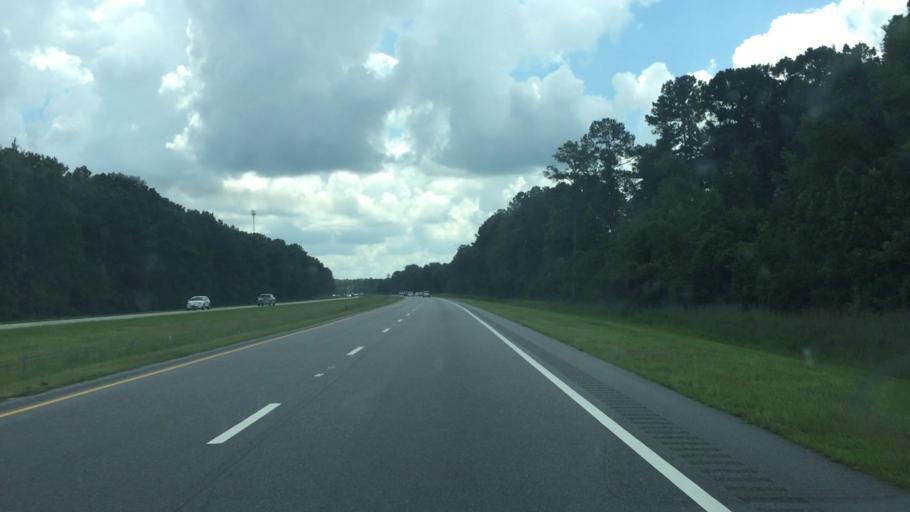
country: US
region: North Carolina
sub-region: Columbus County
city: Chadbourn
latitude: 34.4186
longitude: -78.9387
